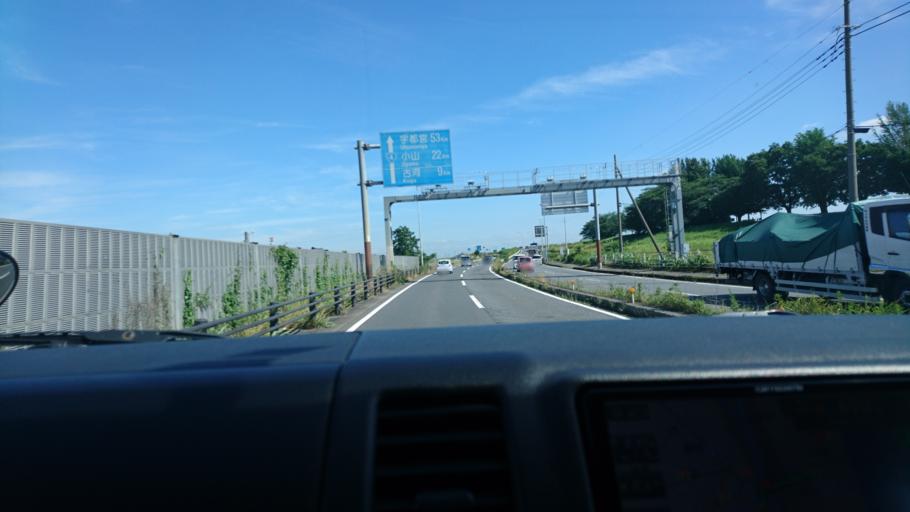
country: JP
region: Saitama
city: Kurihashi
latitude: 36.1356
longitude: 139.7061
